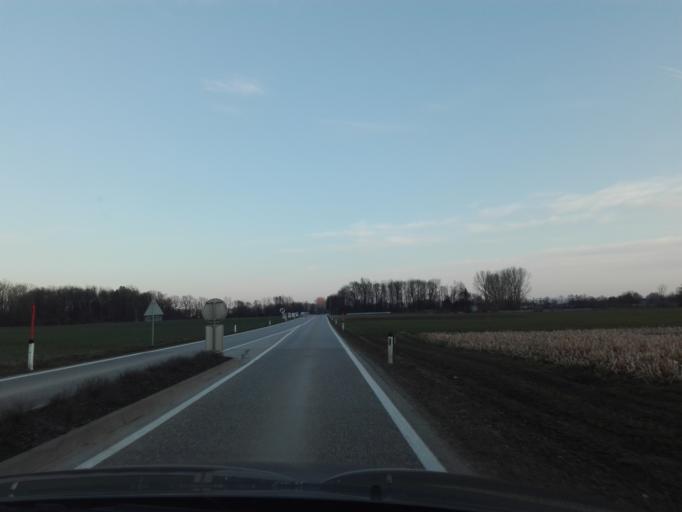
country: AT
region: Upper Austria
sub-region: Politischer Bezirk Urfahr-Umgebung
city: Feldkirchen an der Donau
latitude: 48.3716
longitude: 13.9758
